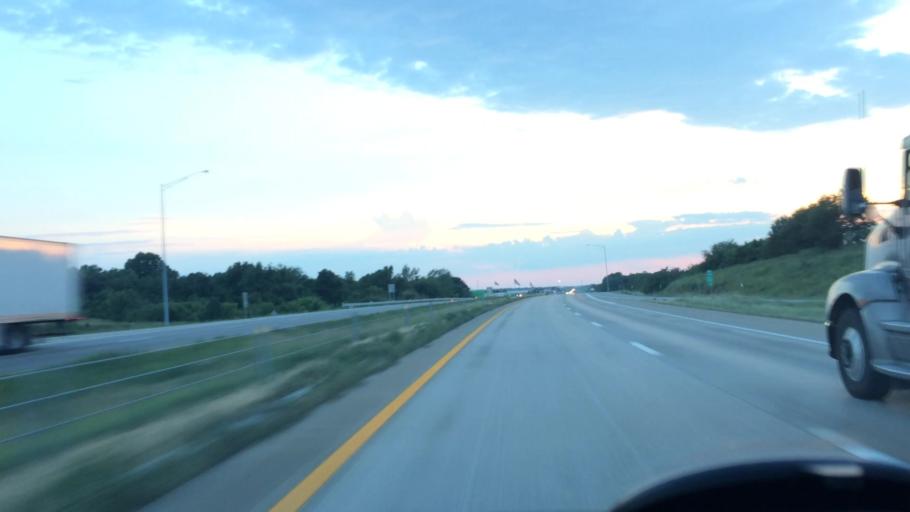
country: US
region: Missouri
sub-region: Greene County
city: Strafford
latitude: 37.2503
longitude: -93.1857
